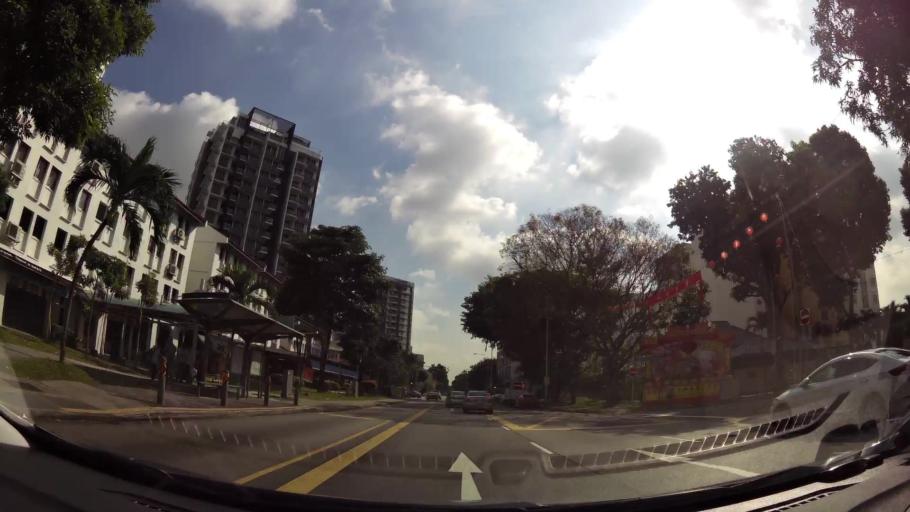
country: SG
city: Singapore
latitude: 1.3157
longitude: 103.8859
